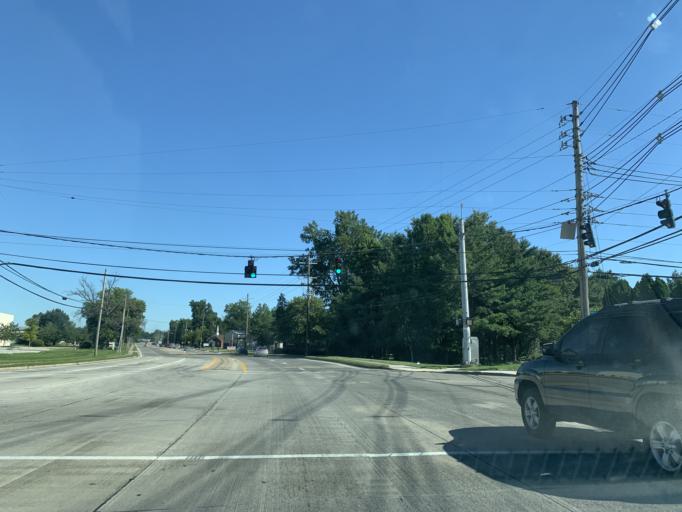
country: US
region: Kentucky
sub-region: Jefferson County
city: Audubon Park
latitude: 38.1829
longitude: -85.6985
